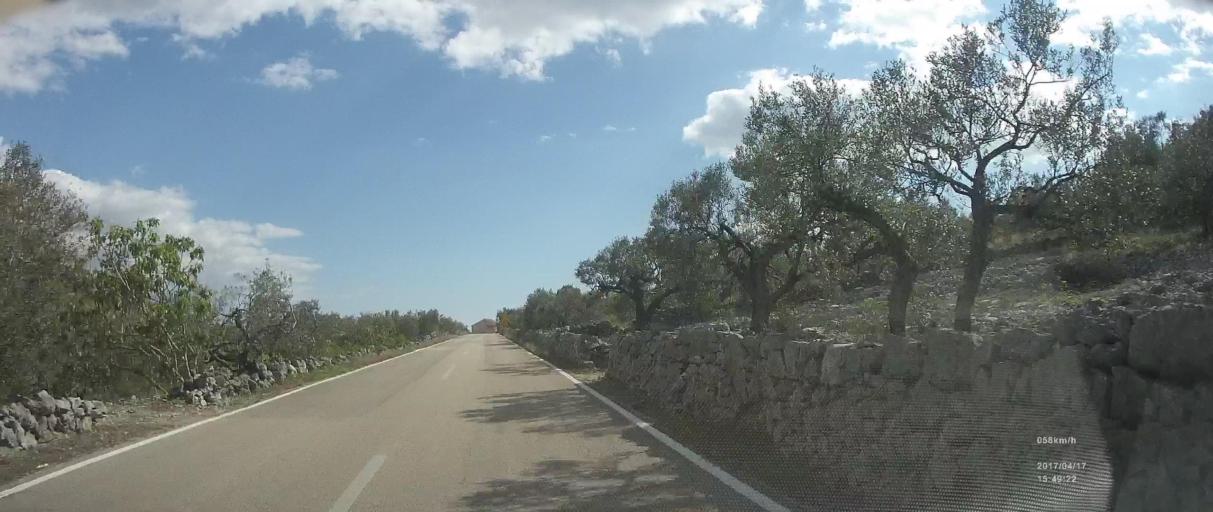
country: HR
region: Sibensko-Kniniska
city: Primosten
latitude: 43.6146
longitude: 15.9762
